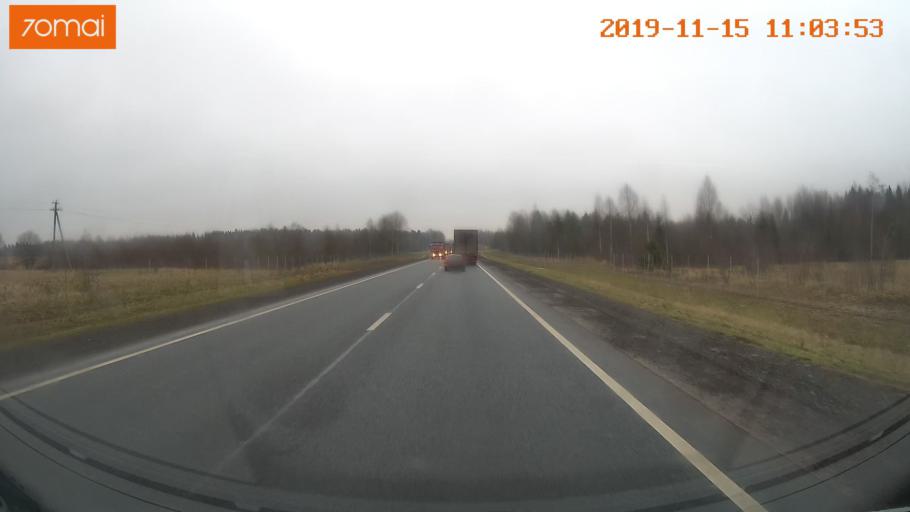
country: RU
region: Vologda
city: Chebsara
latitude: 59.1226
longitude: 38.9719
